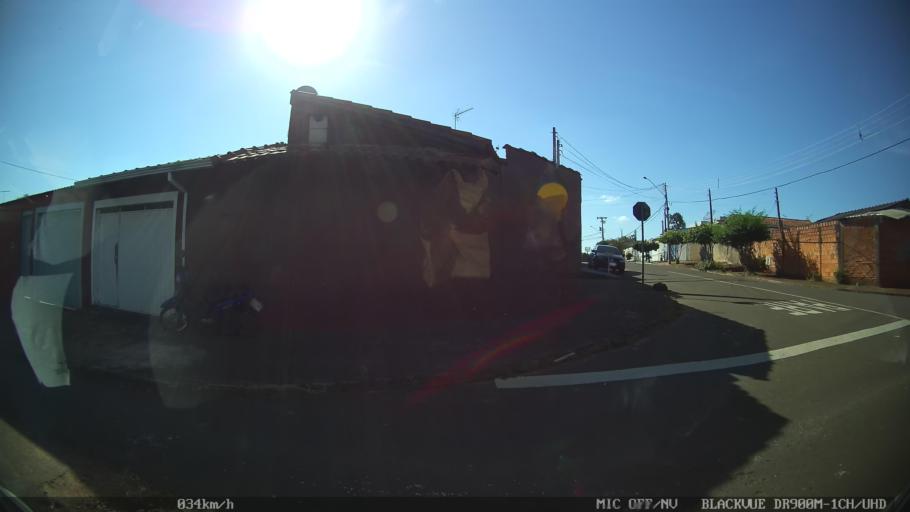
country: BR
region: Sao Paulo
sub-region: Franca
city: Franca
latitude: -20.4918
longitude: -47.4273
